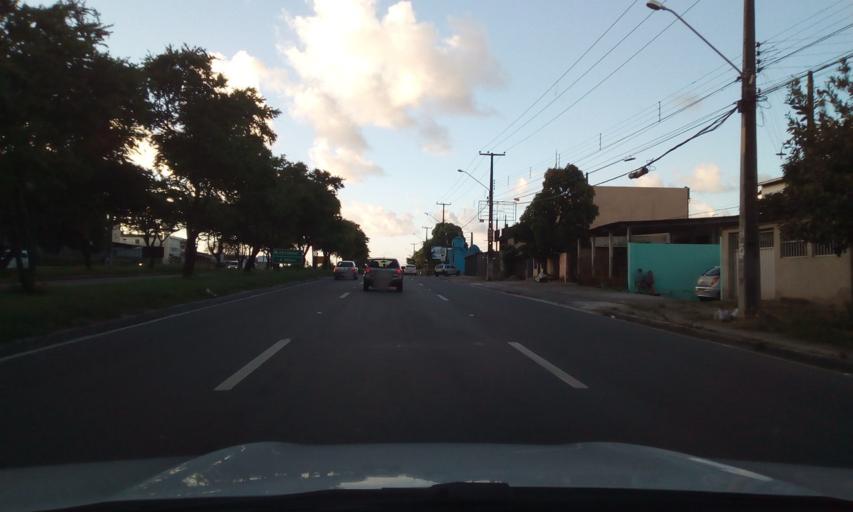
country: BR
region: Pernambuco
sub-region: Igarassu
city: Igarassu
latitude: -7.8613
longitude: -34.9078
